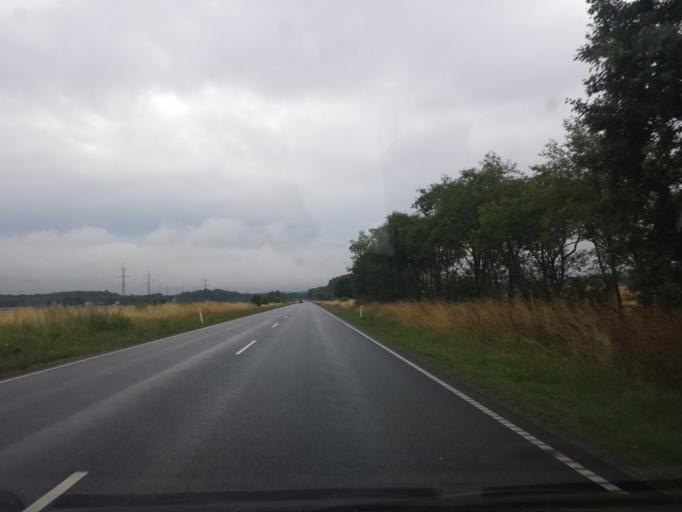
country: DK
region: South Denmark
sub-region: Sonderborg Kommune
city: Sonderborg
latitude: 54.9319
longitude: 9.8260
